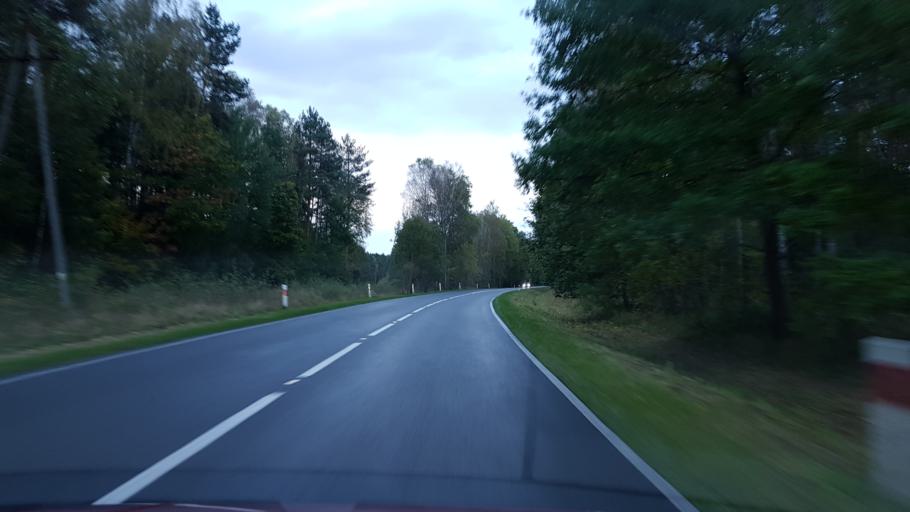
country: PL
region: Greater Poland Voivodeship
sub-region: Powiat zlotowski
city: Tarnowka
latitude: 53.2497
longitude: 16.8946
